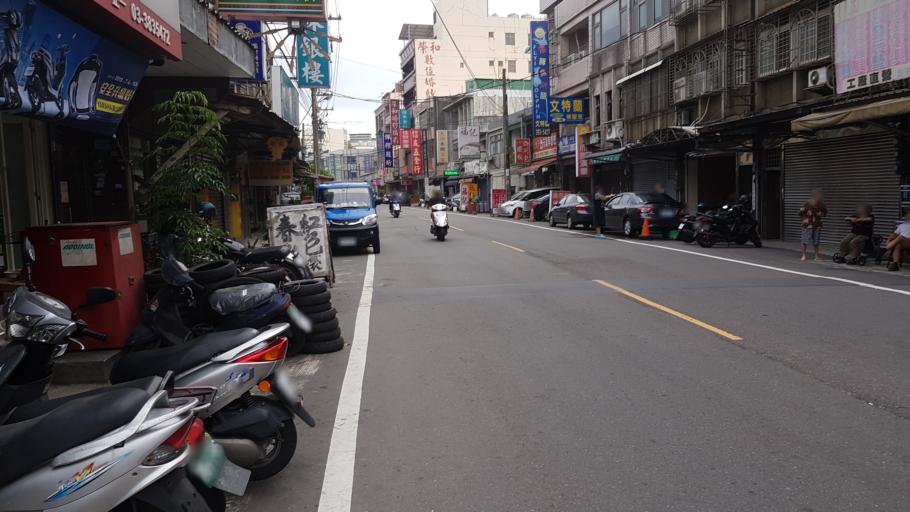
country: TW
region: Taiwan
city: Taoyuan City
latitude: 25.0772
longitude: 121.2578
